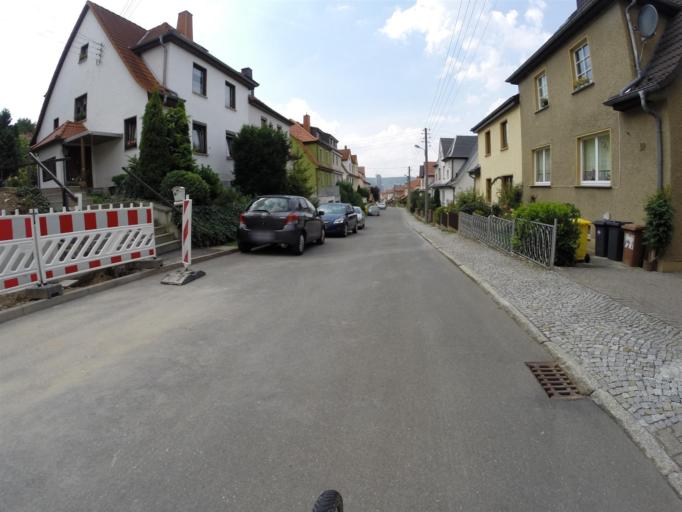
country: DE
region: Thuringia
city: Jena
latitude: 50.9318
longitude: 11.6105
